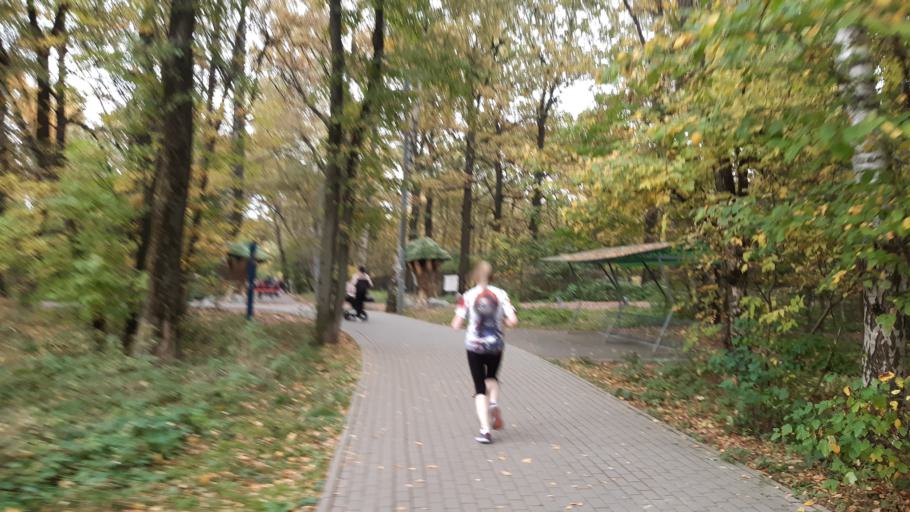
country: RU
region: Moscow
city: Vagonoremont
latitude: 55.9001
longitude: 37.5642
